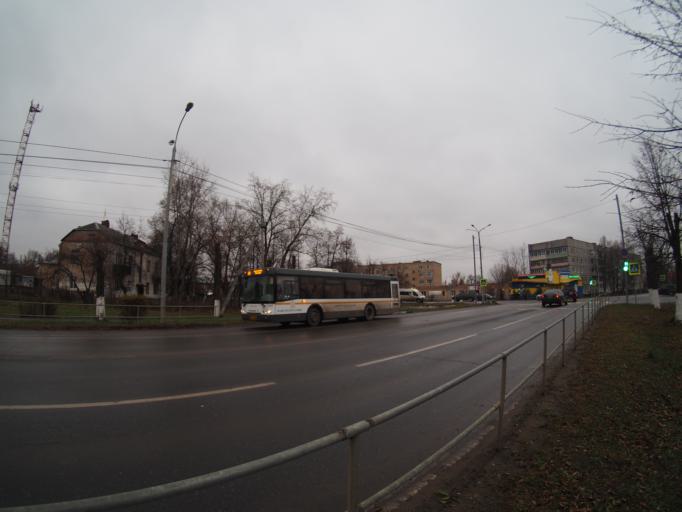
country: RU
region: Moskovskaya
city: Mikhnevo
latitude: 55.1191
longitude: 37.9468
